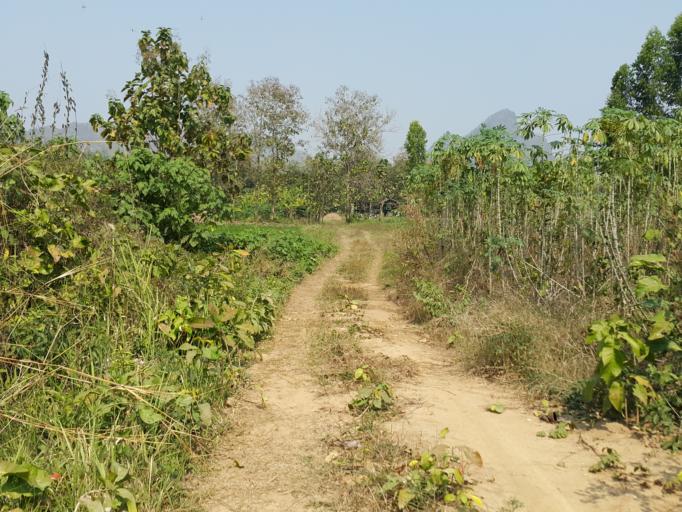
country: TH
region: Sukhothai
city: Thung Saliam
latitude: 17.3274
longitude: 99.4923
